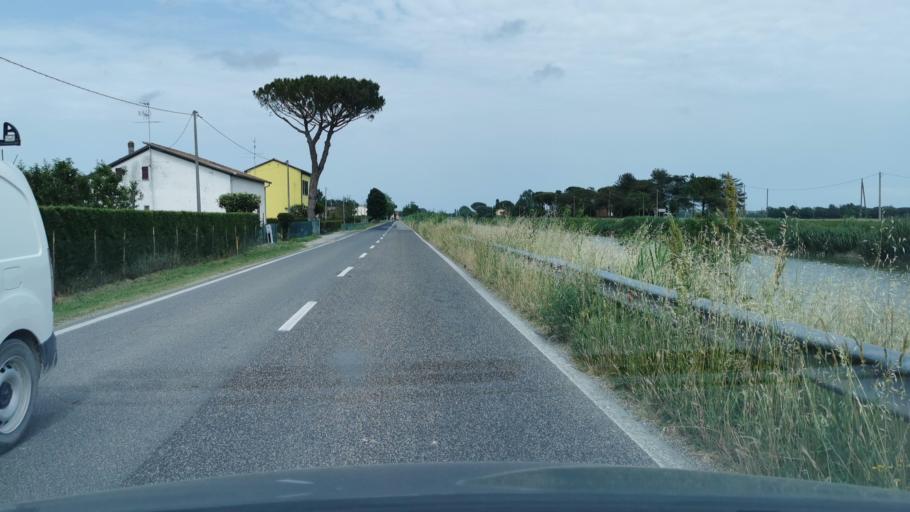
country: IT
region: Emilia-Romagna
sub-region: Provincia di Ravenna
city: Sant'Alberto
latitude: 44.5481
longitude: 12.2149
